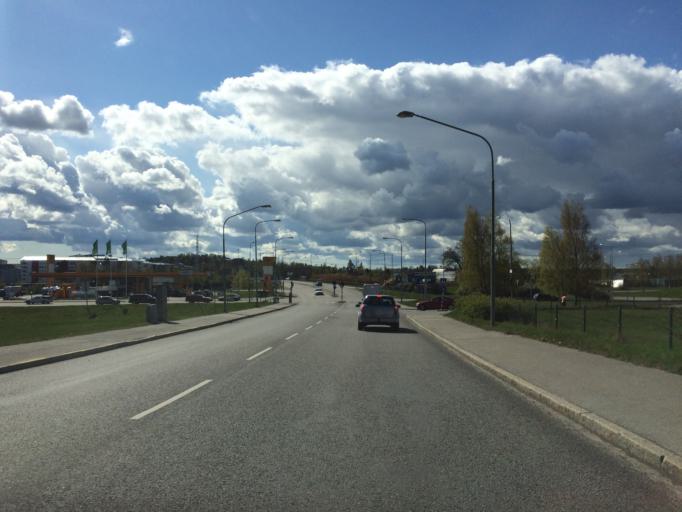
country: SE
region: Stockholm
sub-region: Huddinge Kommun
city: Segeltorp
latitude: 59.2906
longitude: 17.9466
